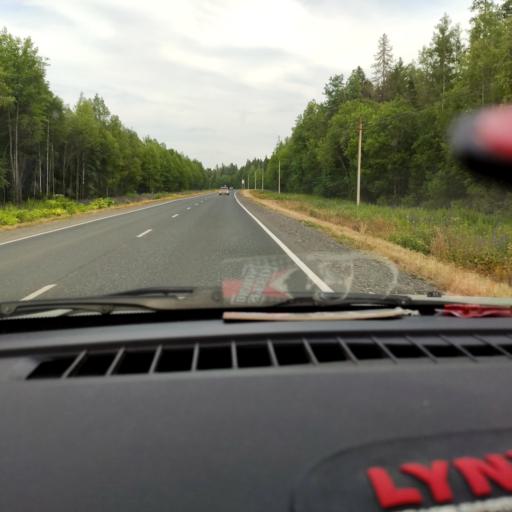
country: RU
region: Perm
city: Polazna
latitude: 58.1954
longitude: 56.2672
